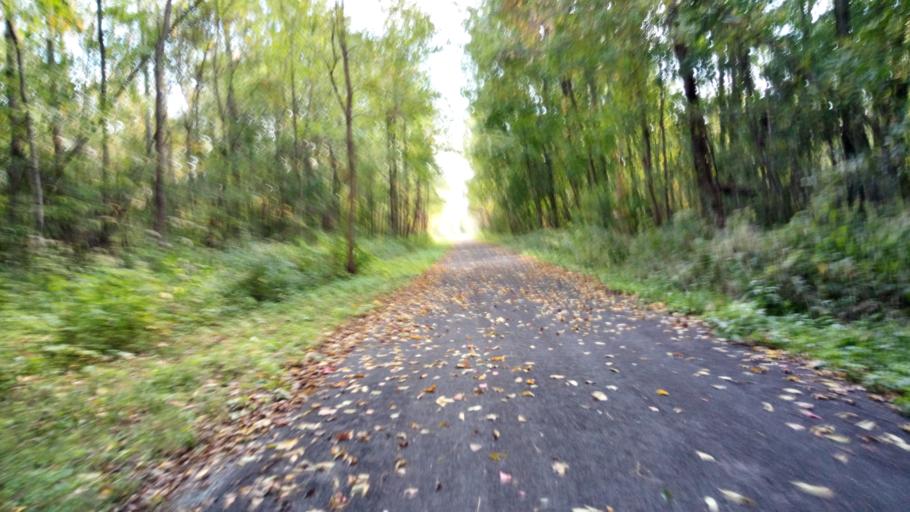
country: US
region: New York
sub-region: Wayne County
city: Clyde
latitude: 43.0744
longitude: -76.8615
